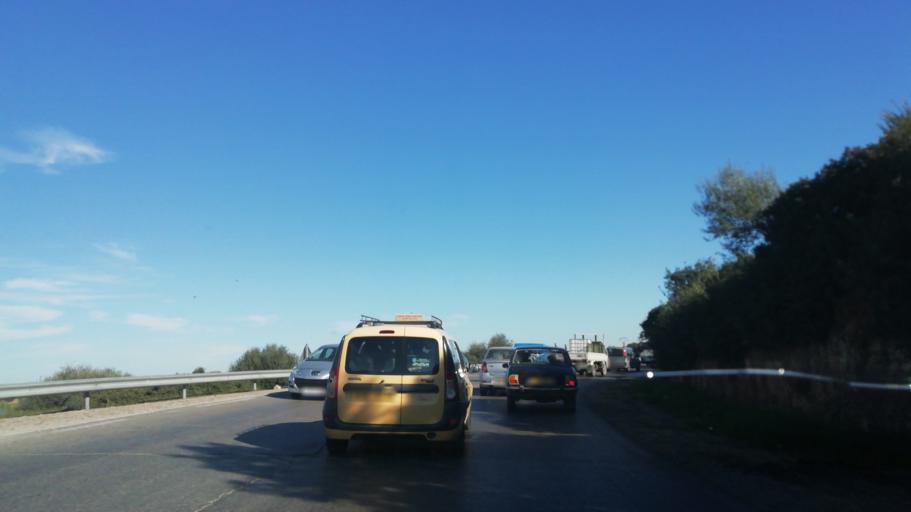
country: DZ
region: Relizane
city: Smala
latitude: 35.7010
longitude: 0.7750
